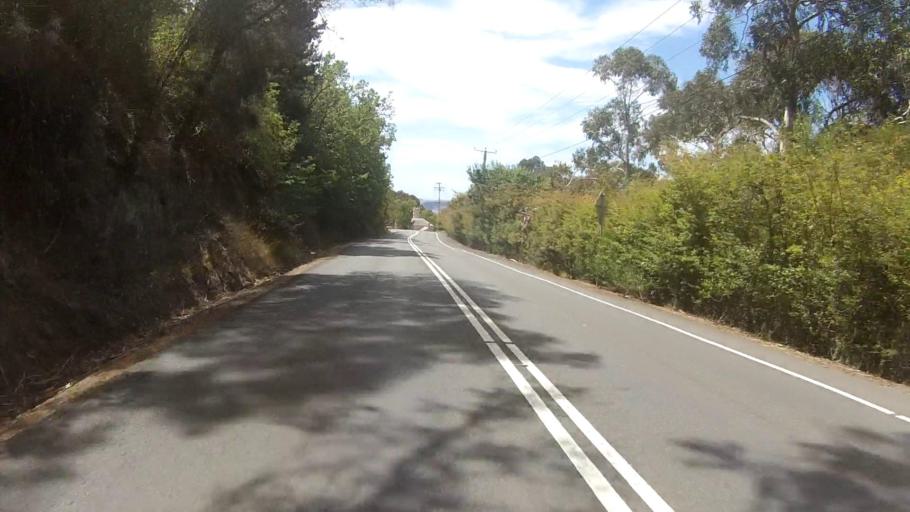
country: AU
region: Tasmania
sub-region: Kingborough
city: Taroona
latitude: -42.9590
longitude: 147.3353
